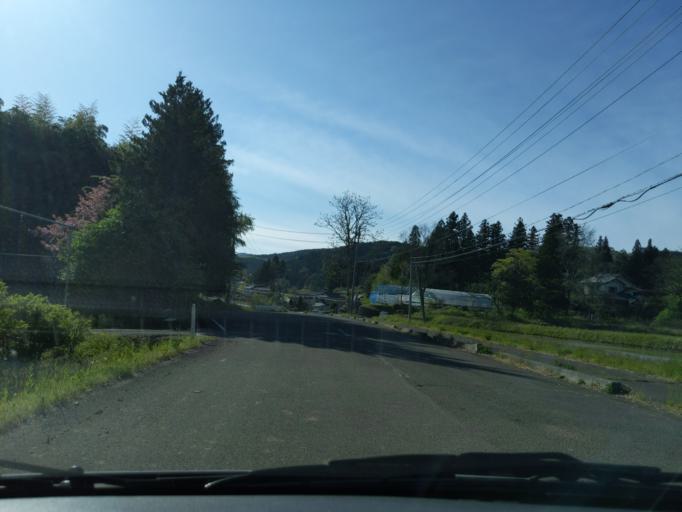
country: JP
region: Iwate
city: Ichinoseki
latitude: 38.8748
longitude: 140.8947
